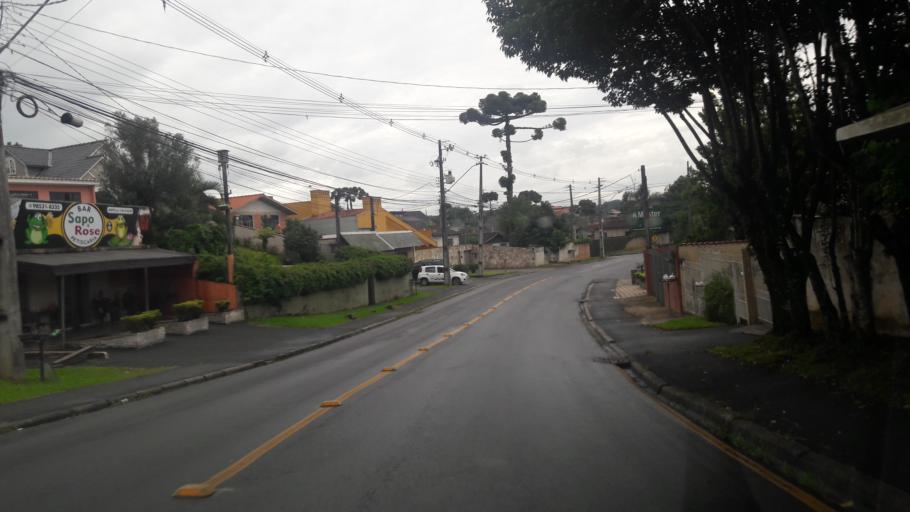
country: BR
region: Parana
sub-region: Curitiba
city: Curitiba
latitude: -25.4012
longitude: -49.3267
